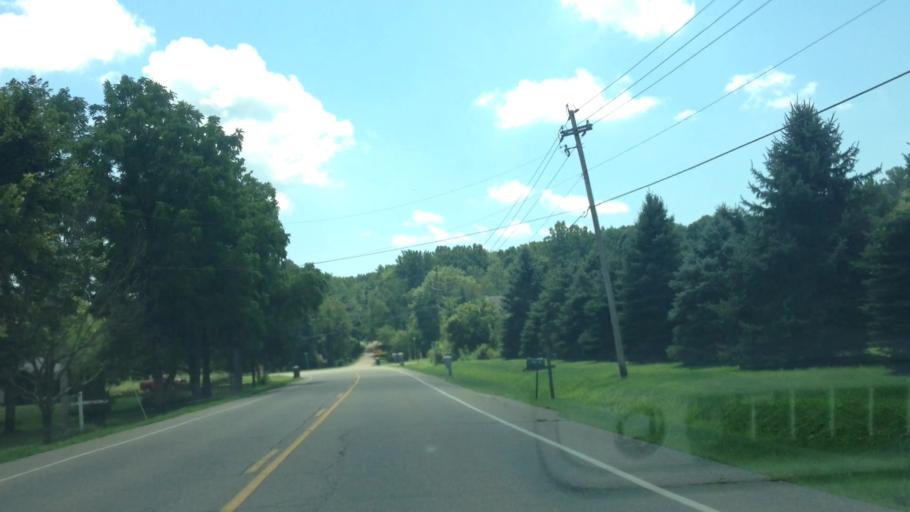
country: US
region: Ohio
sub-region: Summit County
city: Clinton
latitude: 40.9515
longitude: -81.6320
